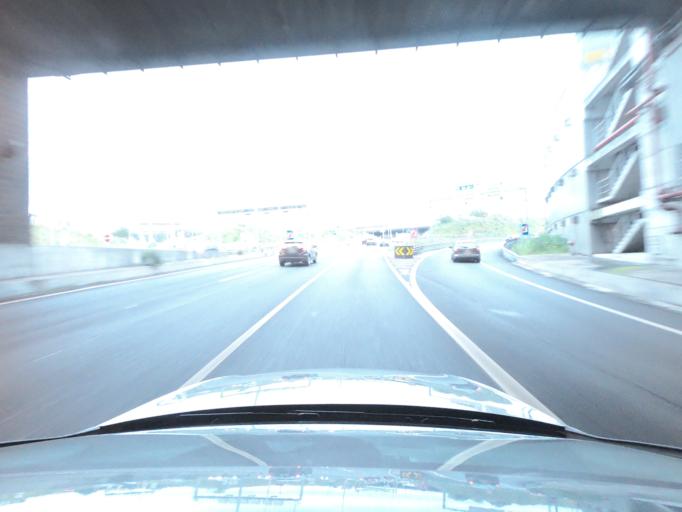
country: PT
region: Lisbon
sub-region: Odivelas
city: Pontinha
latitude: 38.7433
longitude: -9.2045
